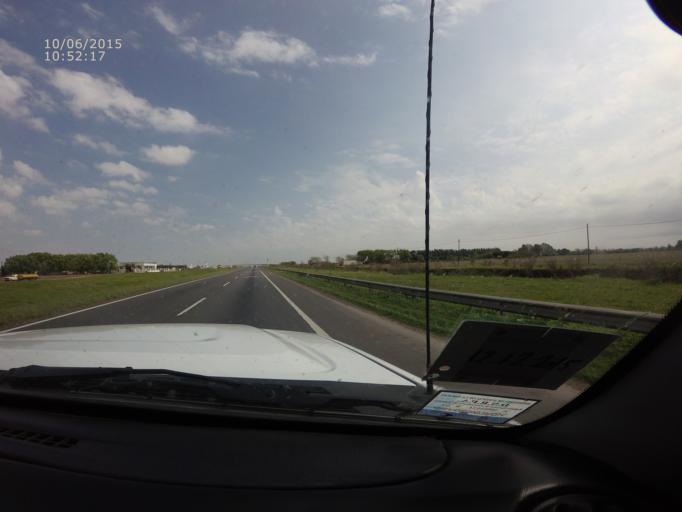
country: AR
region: Buenos Aires
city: San Nicolas de los Arroyos
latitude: -33.3541
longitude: -60.2683
